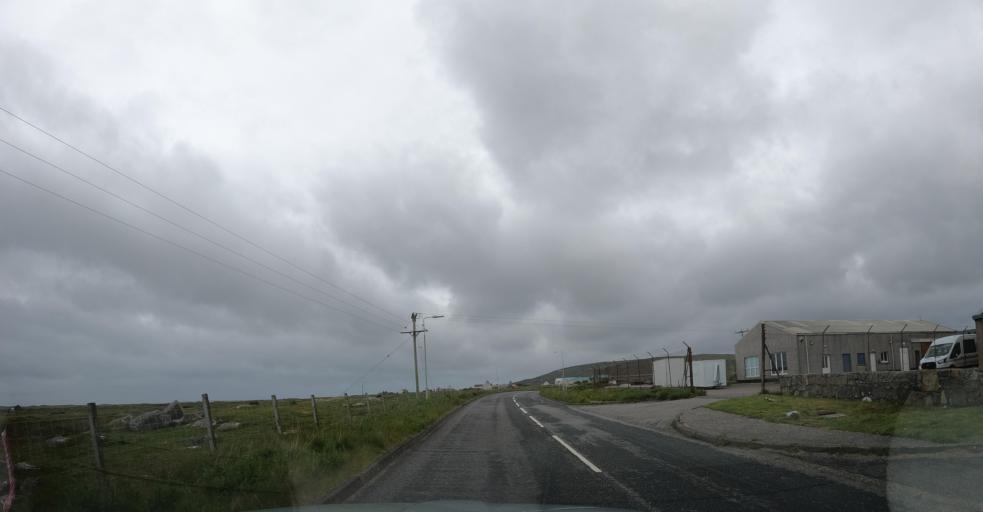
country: GB
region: Scotland
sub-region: Eilean Siar
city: Isle of South Uist
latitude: 57.1697
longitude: -7.3744
